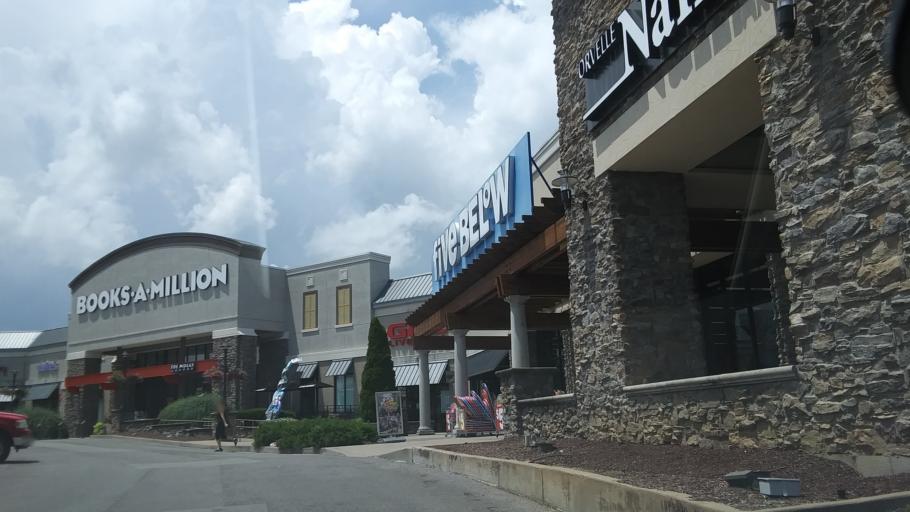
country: US
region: Tennessee
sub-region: Davidson County
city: Belle Meade
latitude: 36.1380
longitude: -86.8874
